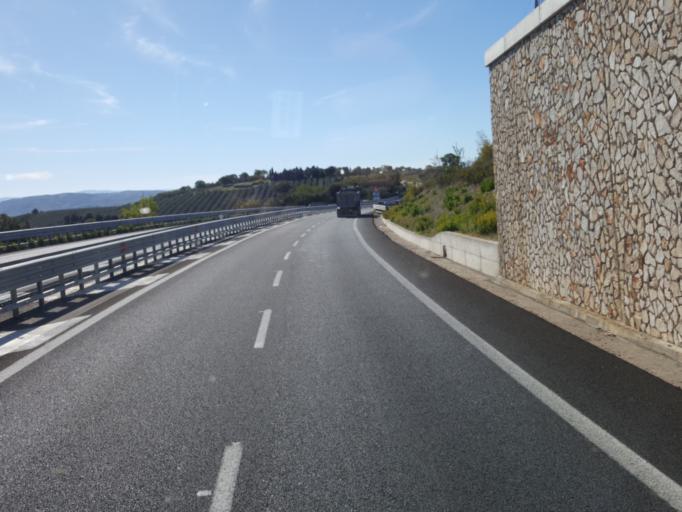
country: IT
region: Tuscany
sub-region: Provincia di Grosseto
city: Civitella Marittima
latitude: 42.9940
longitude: 11.2892
